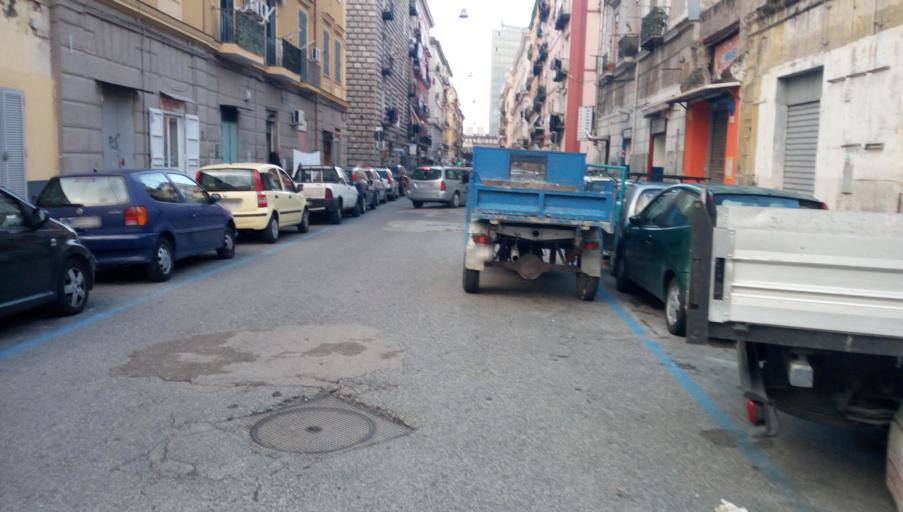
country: IT
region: Campania
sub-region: Provincia di Napoli
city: Napoli
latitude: 40.8572
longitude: 14.2719
